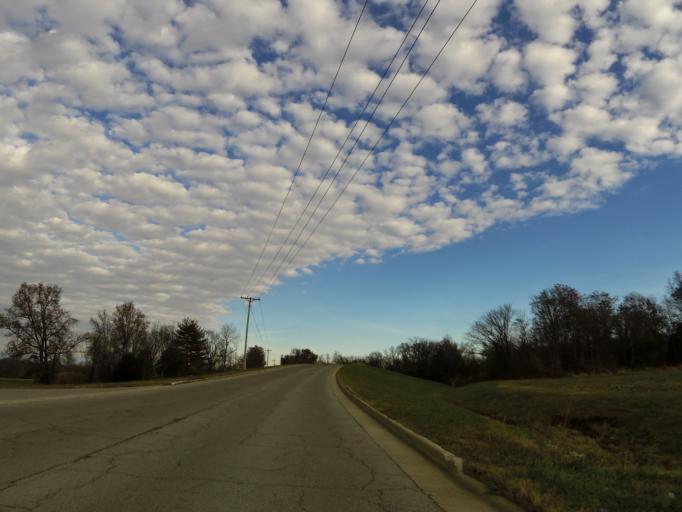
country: US
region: Illinois
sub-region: Jefferson County
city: Mount Vernon
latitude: 38.3407
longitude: -88.9698
